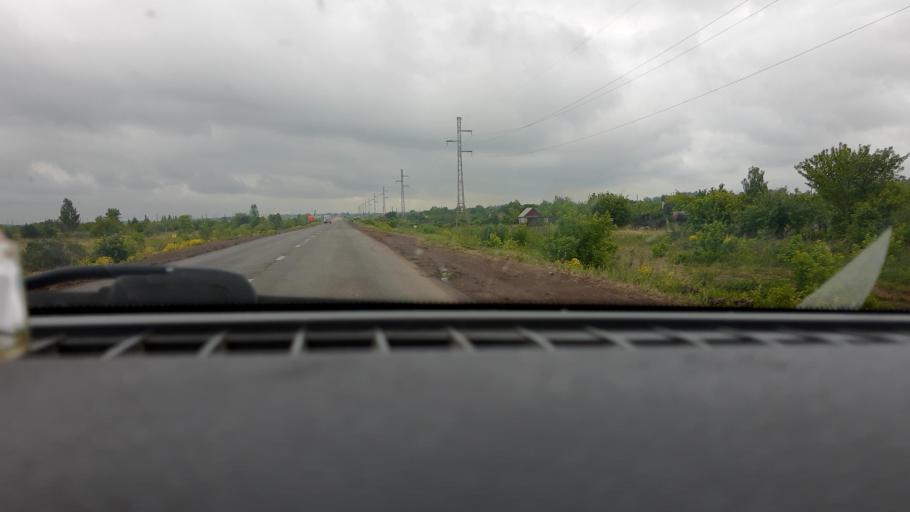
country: RU
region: Bashkortostan
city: Priyutovo
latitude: 53.9112
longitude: 53.9478
